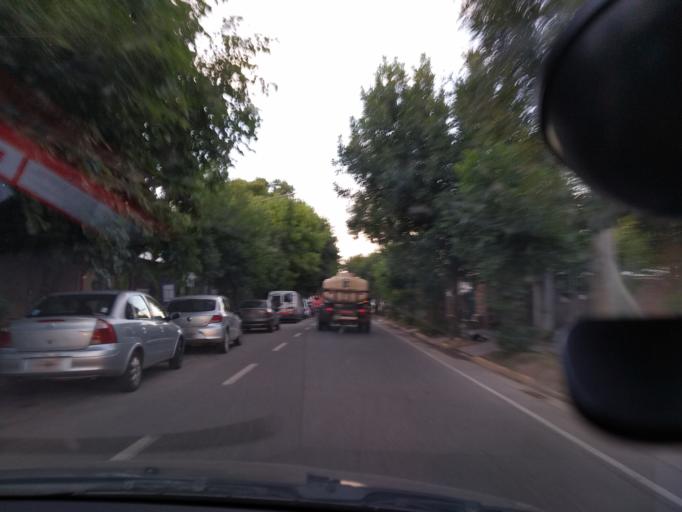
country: AR
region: Cordoba
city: Villa Las Rosas
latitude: -31.9484
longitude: -65.0519
